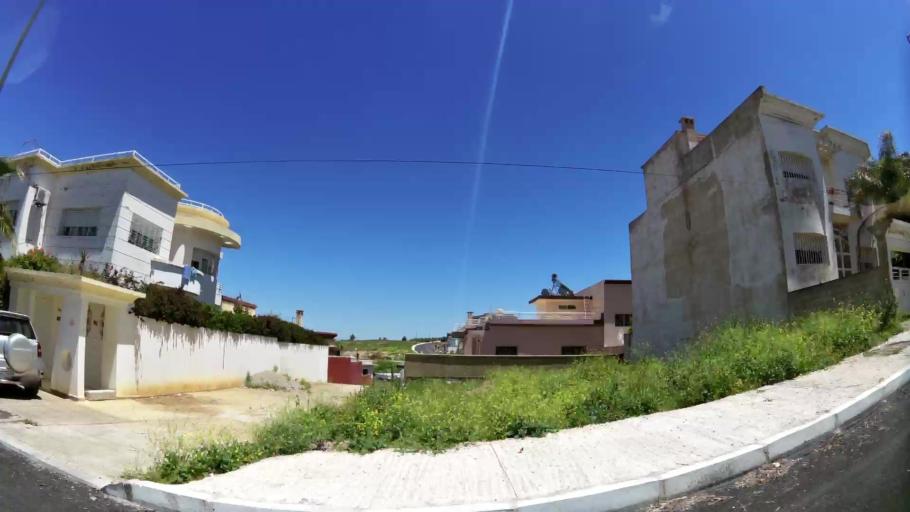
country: MA
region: Meknes-Tafilalet
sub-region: Meknes
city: Meknes
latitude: 33.9108
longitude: -5.5542
